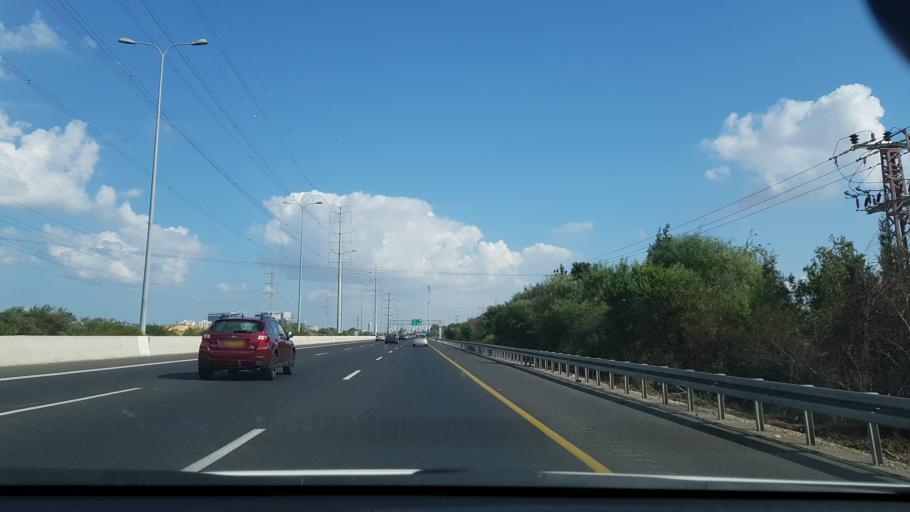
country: IL
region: Central District
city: Rishon LeZiyyon
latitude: 31.9889
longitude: 34.7974
